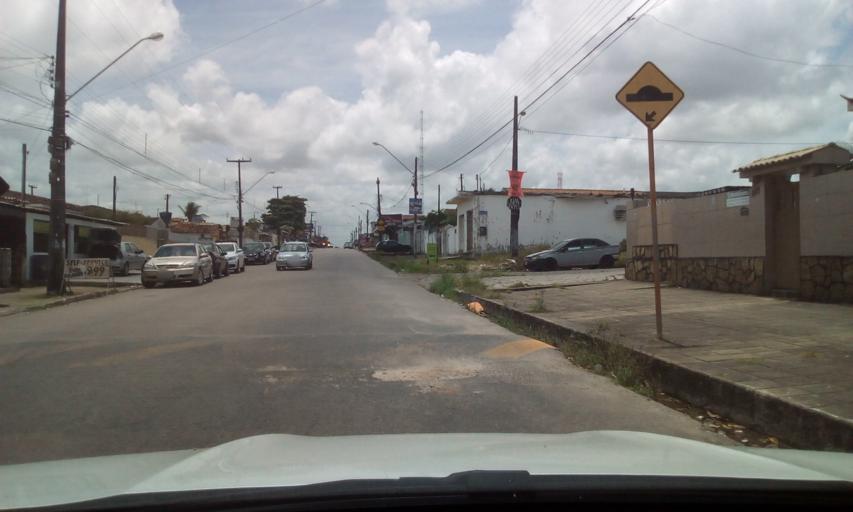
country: BR
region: Paraiba
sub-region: Bayeux
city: Bayeux
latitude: -7.1751
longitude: -34.8907
